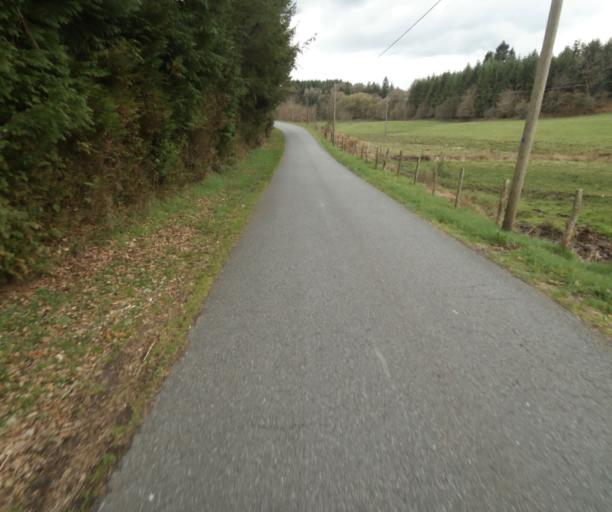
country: FR
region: Limousin
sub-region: Departement de la Correze
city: Correze
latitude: 45.3070
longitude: 1.9317
